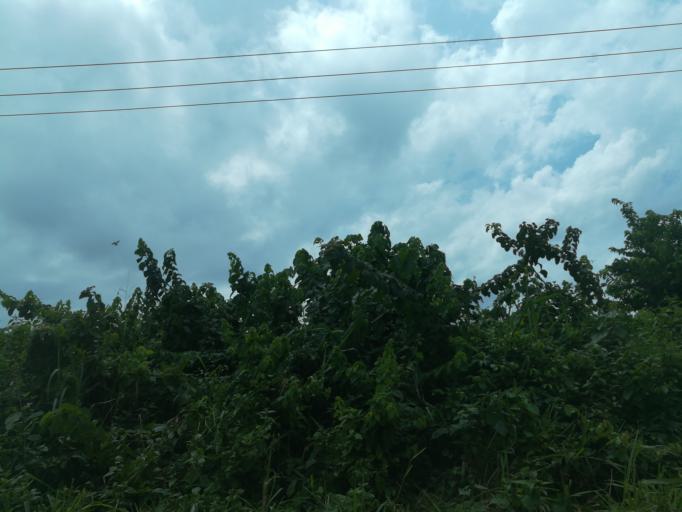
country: NG
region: Lagos
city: Ejirin
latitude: 6.6347
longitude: 3.7091
